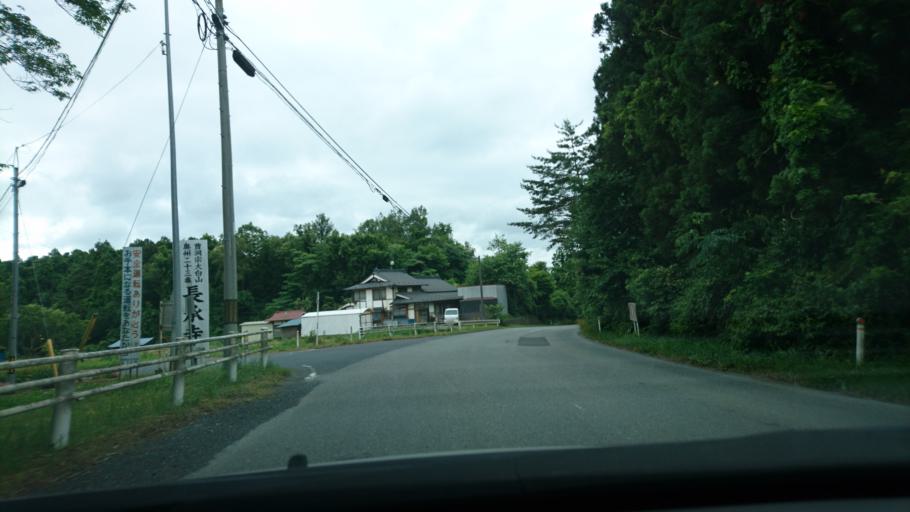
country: JP
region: Iwate
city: Ichinoseki
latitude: 38.7608
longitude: 141.2578
